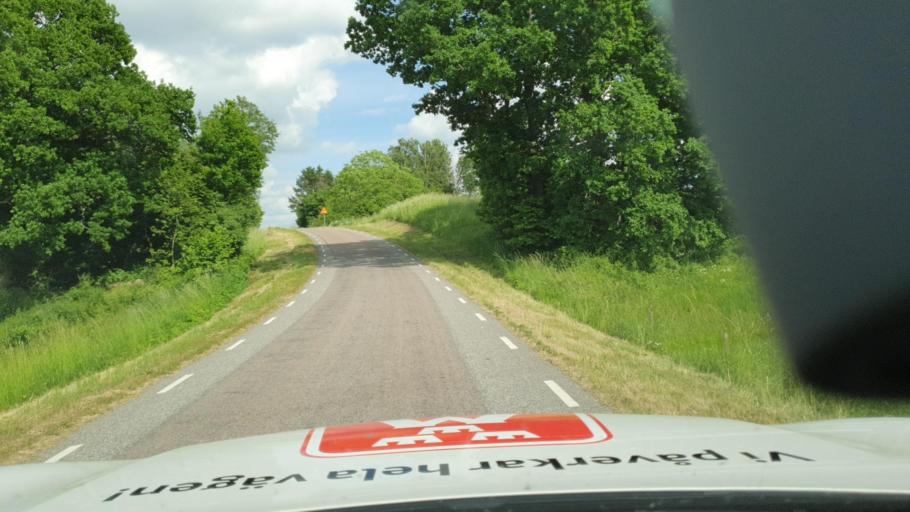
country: SE
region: Skane
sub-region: Skurups Kommun
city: Skurup
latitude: 55.5244
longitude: 13.4514
